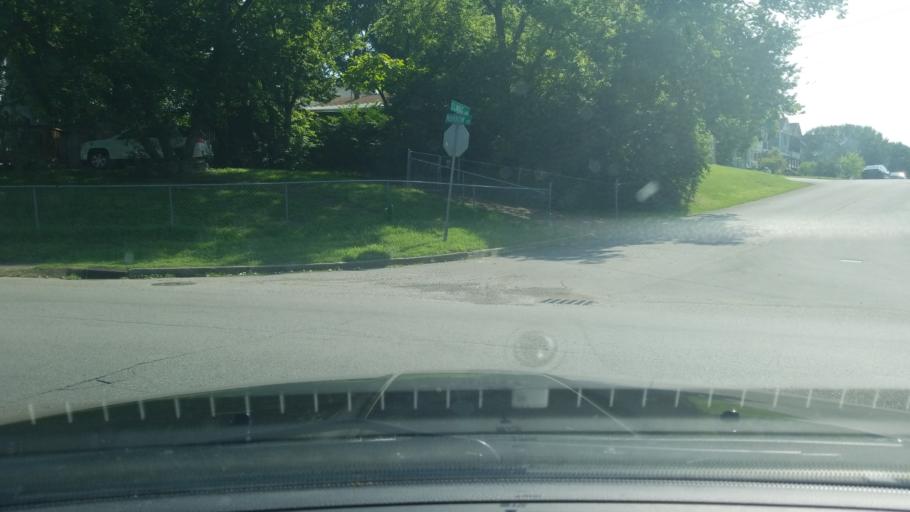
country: US
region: Tennessee
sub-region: Davidson County
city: Belle Meade
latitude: 36.1574
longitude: -86.8535
